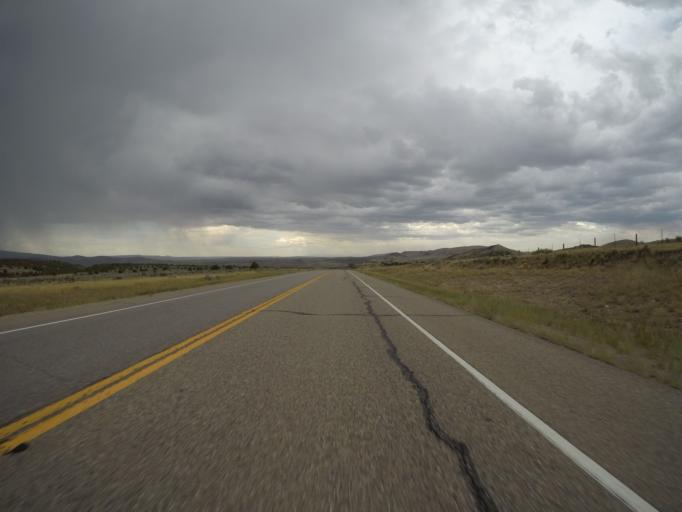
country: US
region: Colorado
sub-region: Rio Blanco County
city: Rangely
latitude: 40.3749
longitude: -108.3759
